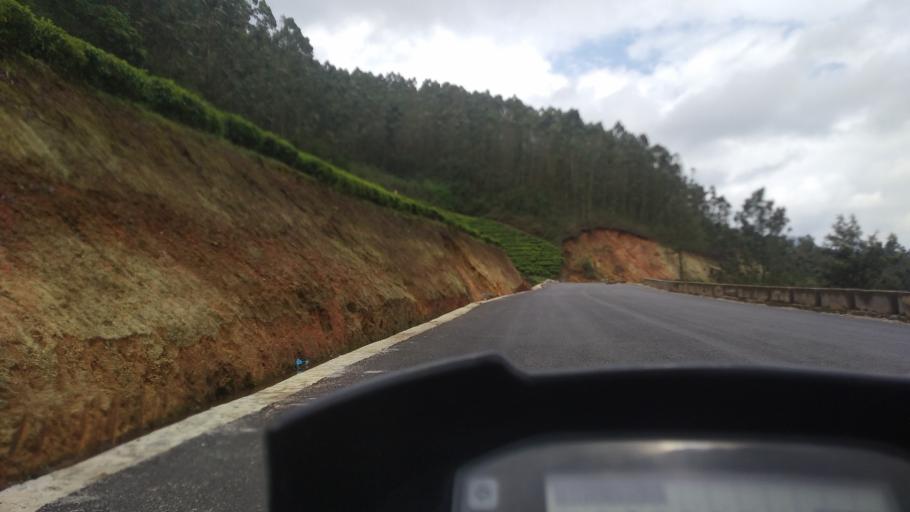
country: IN
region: Kerala
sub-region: Idukki
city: Munnar
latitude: 10.0762
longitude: 77.0881
